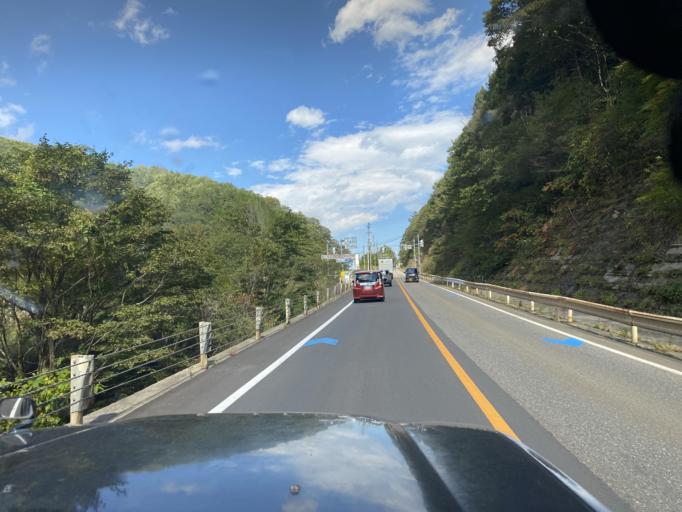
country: JP
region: Nagano
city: Omachi
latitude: 36.5881
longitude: 137.8416
